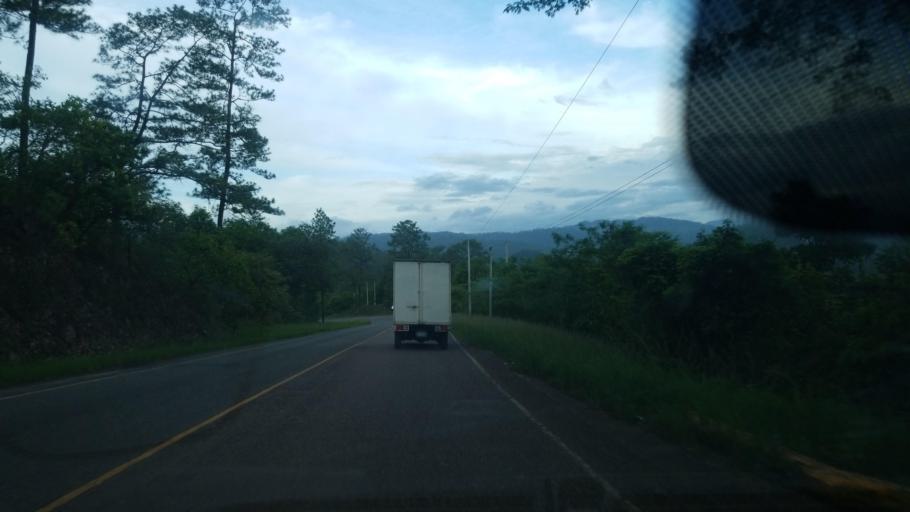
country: HN
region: Santa Barbara
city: Concepcion del Sur
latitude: 14.7997
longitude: -88.1444
